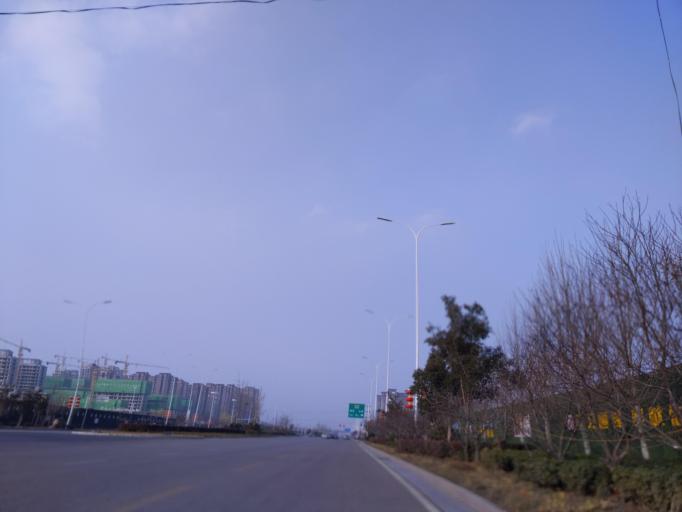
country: CN
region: Henan Sheng
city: Puyang
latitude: 35.8080
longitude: 115.0222
